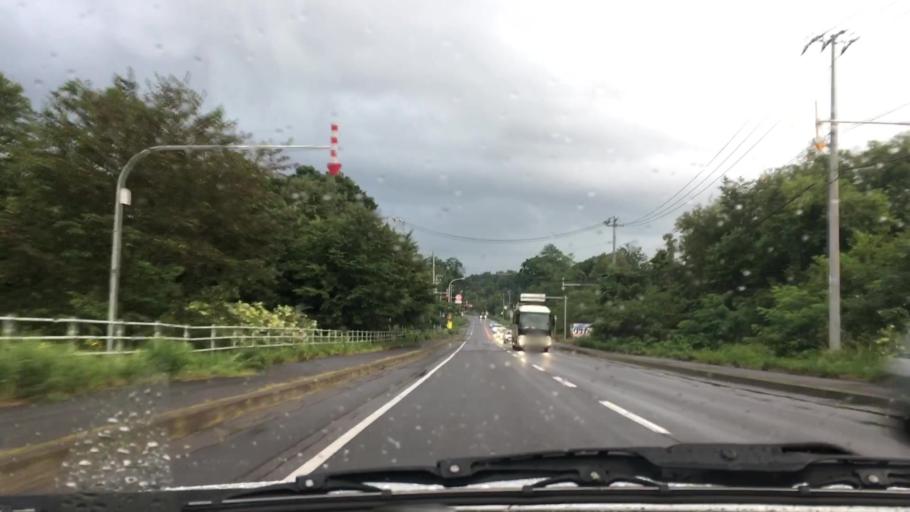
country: JP
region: Hokkaido
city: Nanae
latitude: 42.0860
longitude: 140.5841
